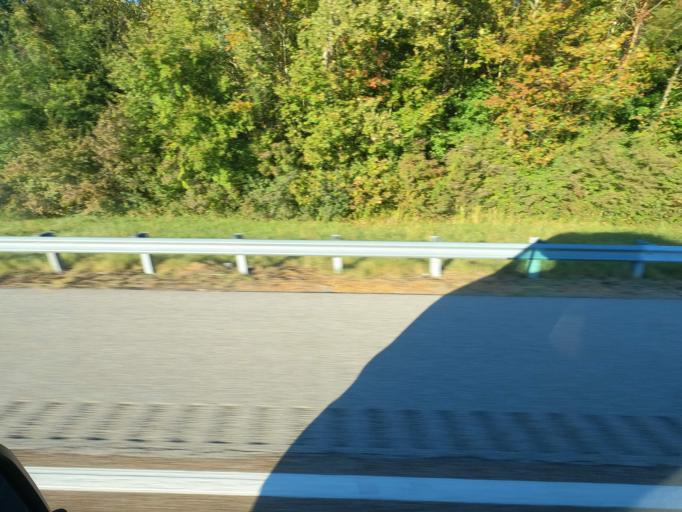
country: US
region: Tennessee
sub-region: Shelby County
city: Millington
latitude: 35.3142
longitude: -89.8646
